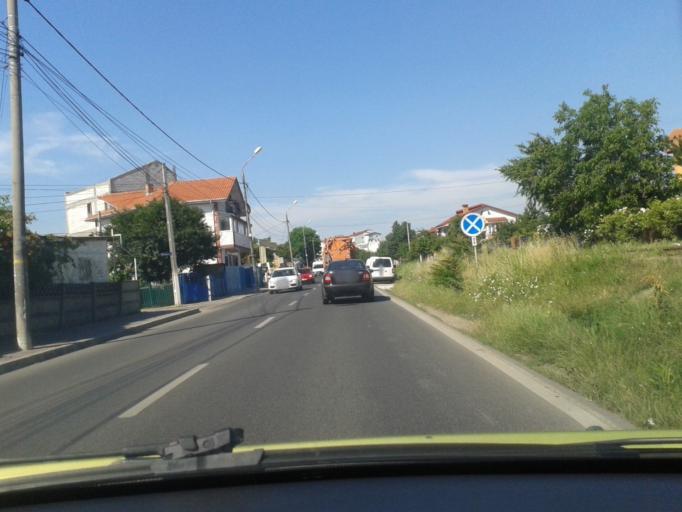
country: RO
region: Constanta
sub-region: Municipiul Mangalia
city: Mangalia
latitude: 43.8152
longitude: 28.5773
